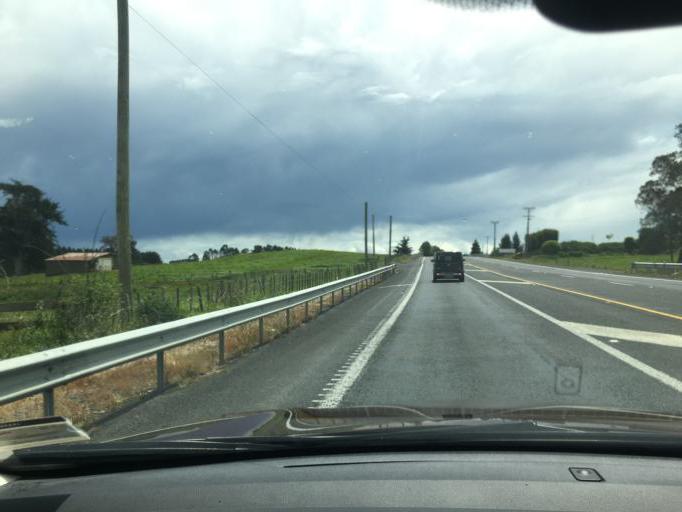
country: NZ
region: Waikato
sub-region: Waipa District
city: Cambridge
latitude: -37.9319
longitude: 175.3130
